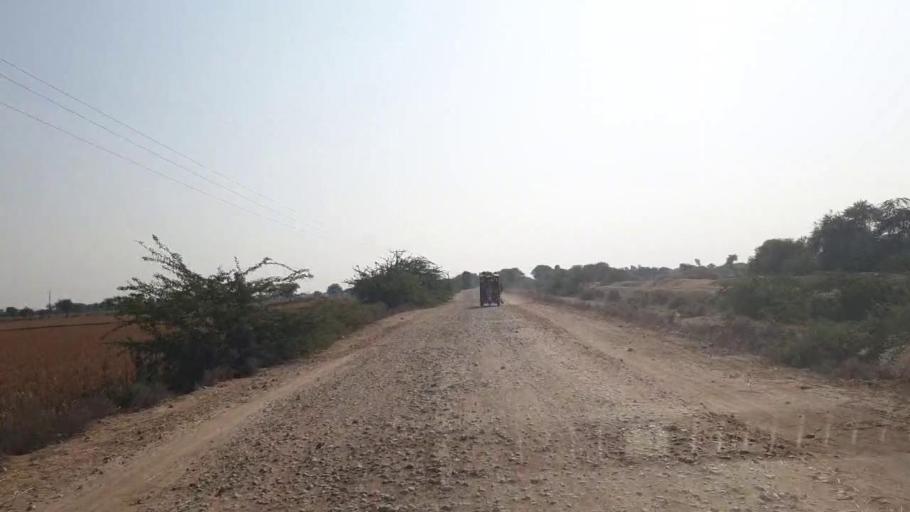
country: PK
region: Sindh
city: Matli
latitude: 24.9251
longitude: 68.6540
